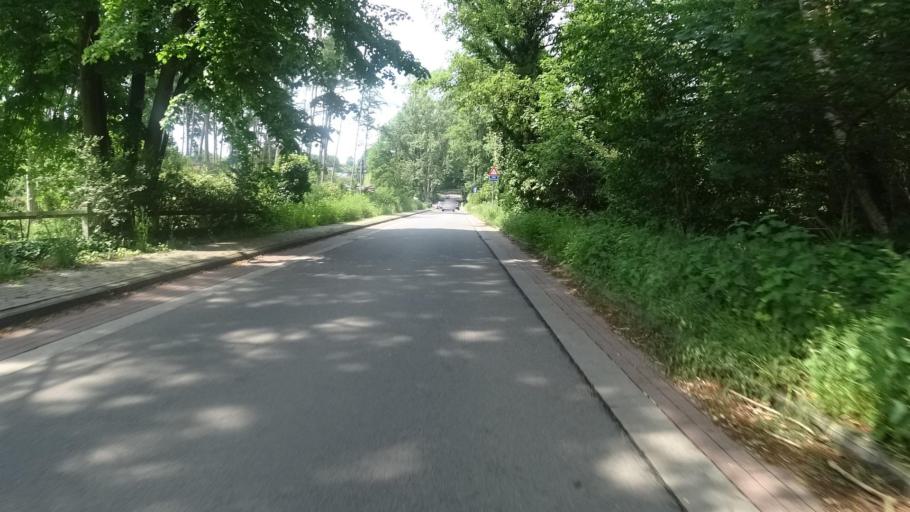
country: BE
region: Wallonia
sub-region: Province du Brabant Wallon
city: Louvain-la-Neuve
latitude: 50.6923
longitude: 4.6305
